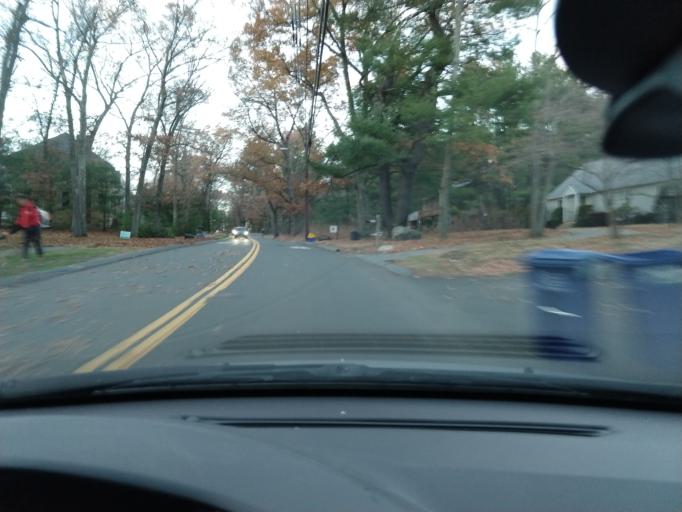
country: US
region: Massachusetts
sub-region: Middlesex County
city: Bedford
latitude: 42.4850
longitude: -71.2398
